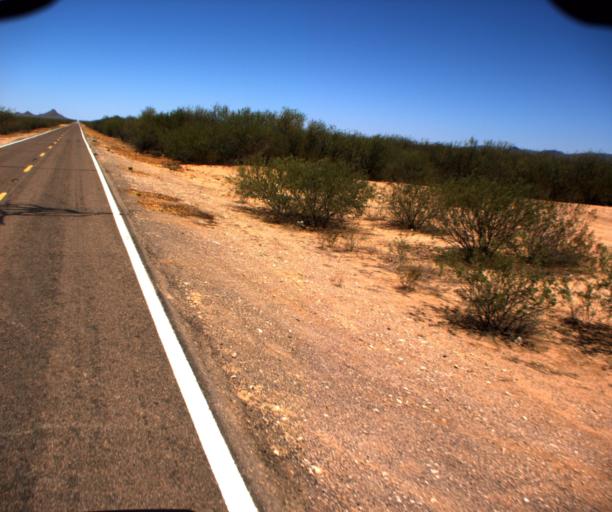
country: US
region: Arizona
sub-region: Pima County
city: Ajo
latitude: 32.1935
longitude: -112.4388
